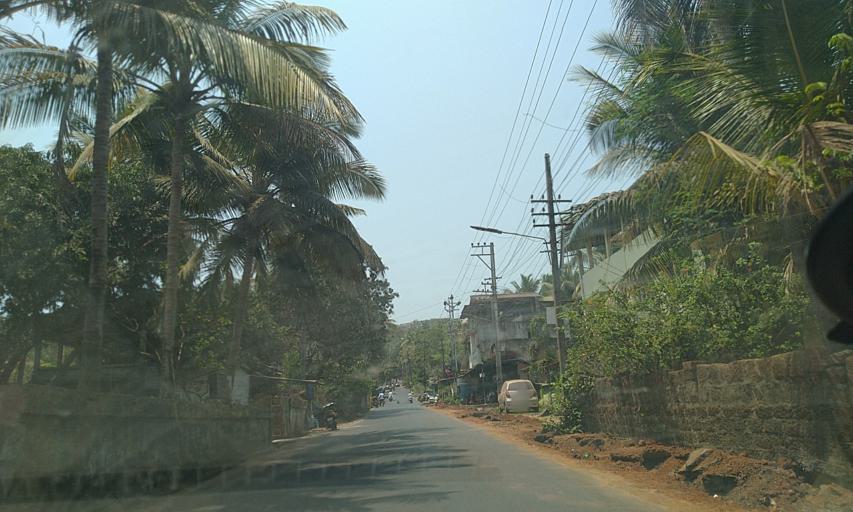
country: IN
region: Goa
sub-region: North Goa
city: Mapuca
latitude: 15.5940
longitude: 73.8018
